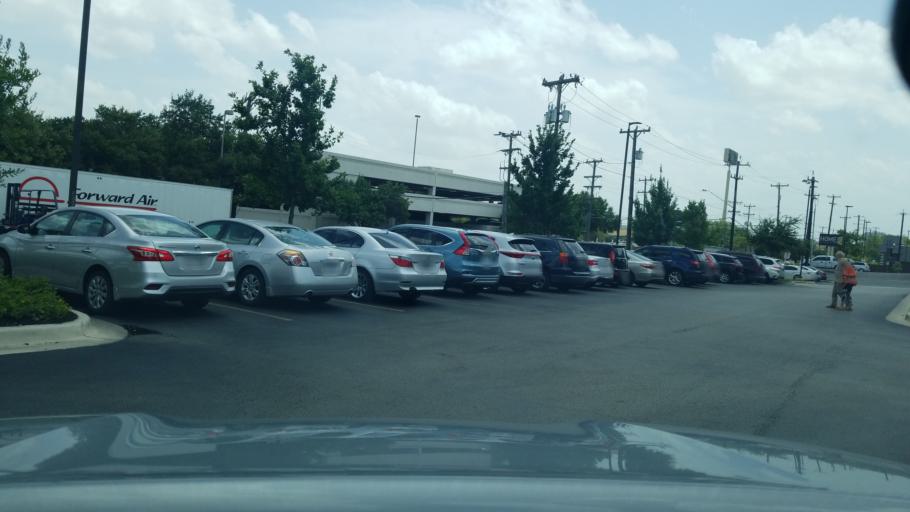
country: US
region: Texas
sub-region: Bexar County
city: Castle Hills
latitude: 29.5197
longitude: -98.4843
